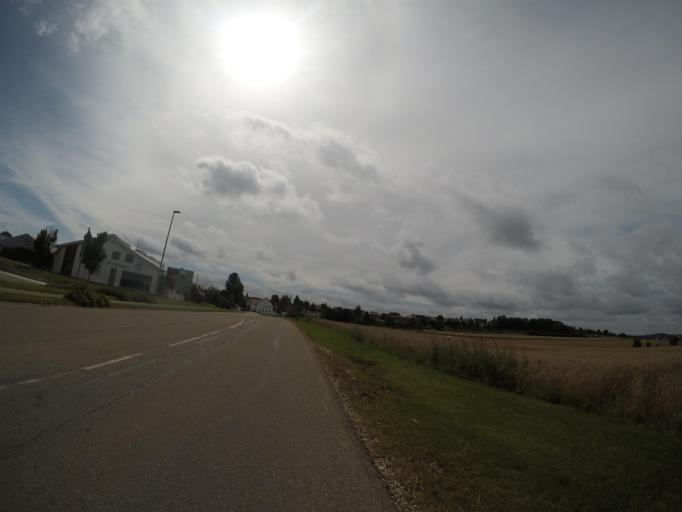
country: DE
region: Baden-Wuerttemberg
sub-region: Tuebingen Region
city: Laichingen
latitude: 48.4500
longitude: 9.6660
